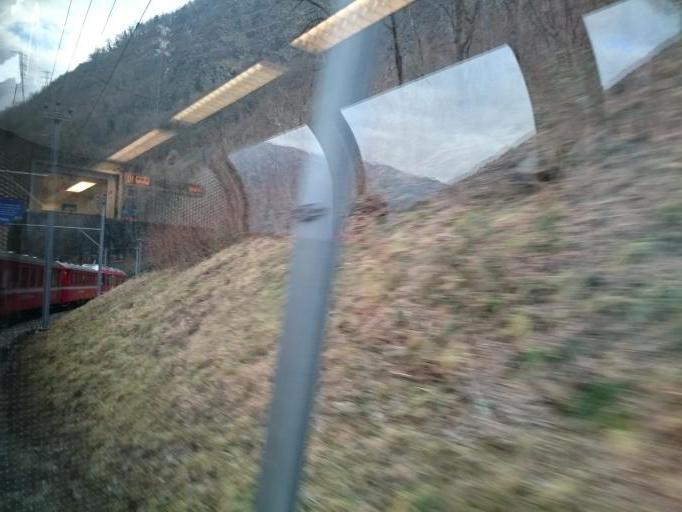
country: IT
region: Lombardy
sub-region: Provincia di Sondrio
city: Tirano
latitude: 46.2277
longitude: 10.1460
